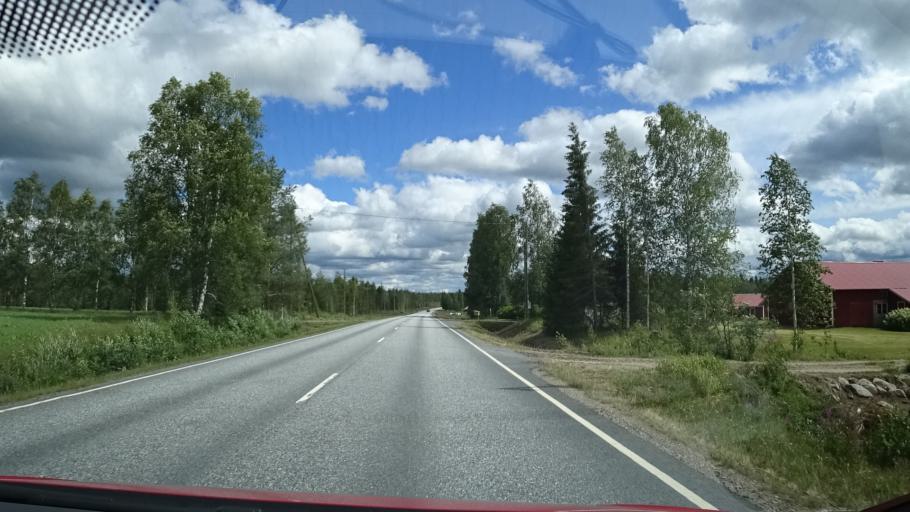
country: FI
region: Northern Savo
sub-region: Koillis-Savo
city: Rautavaara
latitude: 63.3673
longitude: 28.5721
